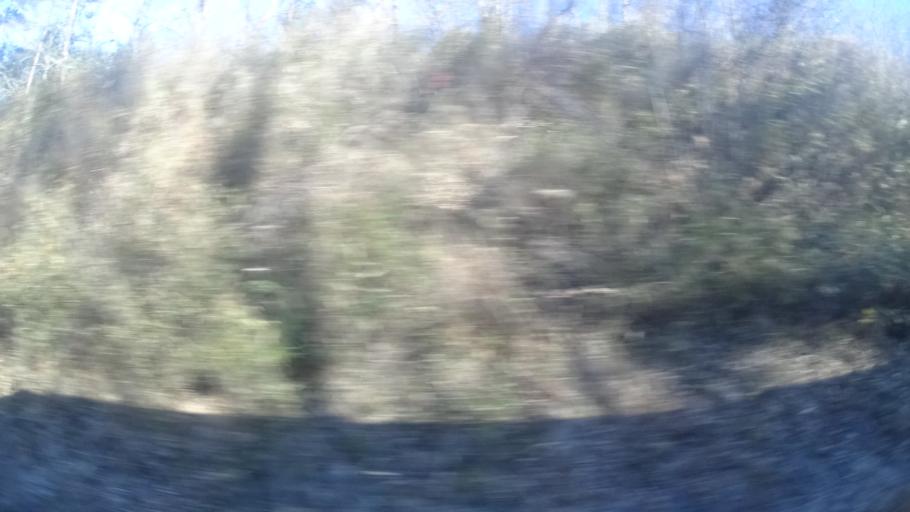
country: JP
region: Miyagi
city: Marumori
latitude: 37.7501
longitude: 140.9387
